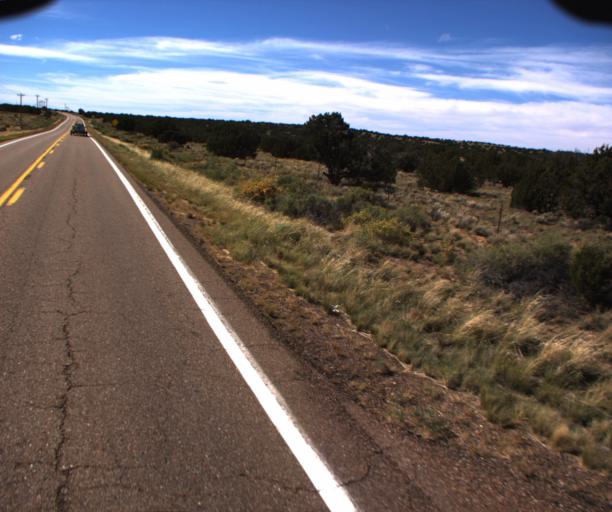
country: US
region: Arizona
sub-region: Apache County
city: Saint Johns
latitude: 34.4850
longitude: -109.5509
